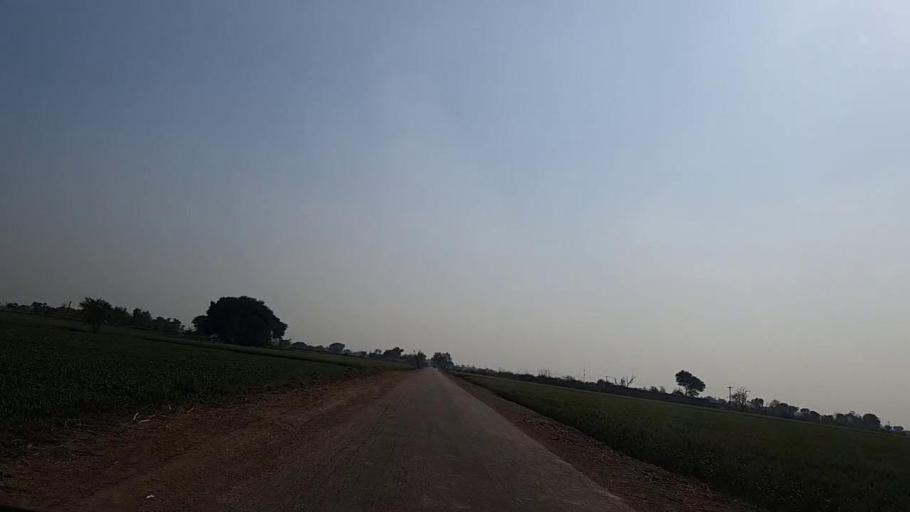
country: PK
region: Sindh
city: Sakrand
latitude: 26.0845
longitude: 68.2901
